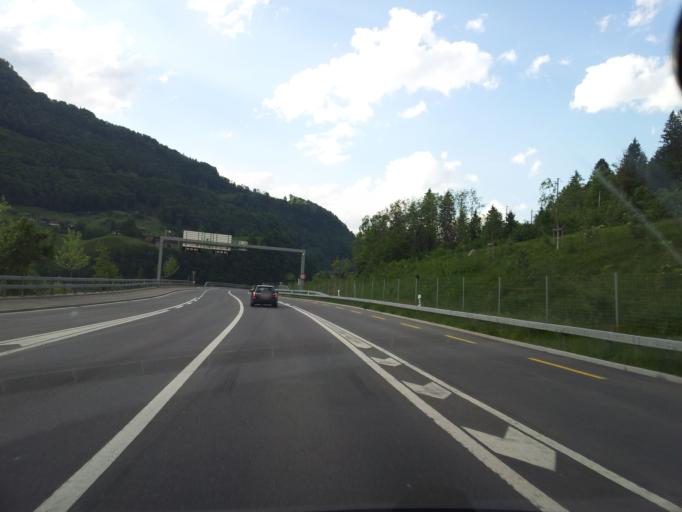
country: CH
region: Obwalden
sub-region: Obwalden
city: Lungern
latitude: 46.8027
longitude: 8.1697
